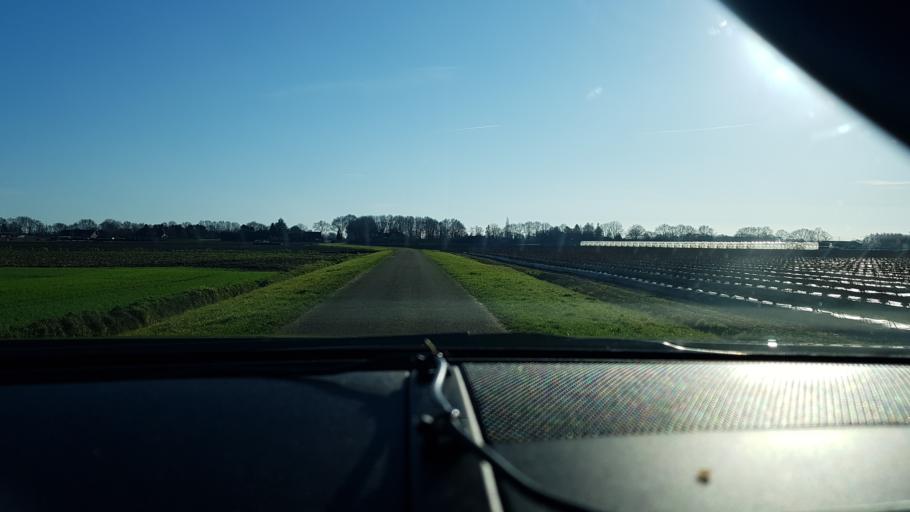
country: NL
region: Limburg
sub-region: Gemeente Leudal
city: Haelen
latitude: 51.2755
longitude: 5.9863
